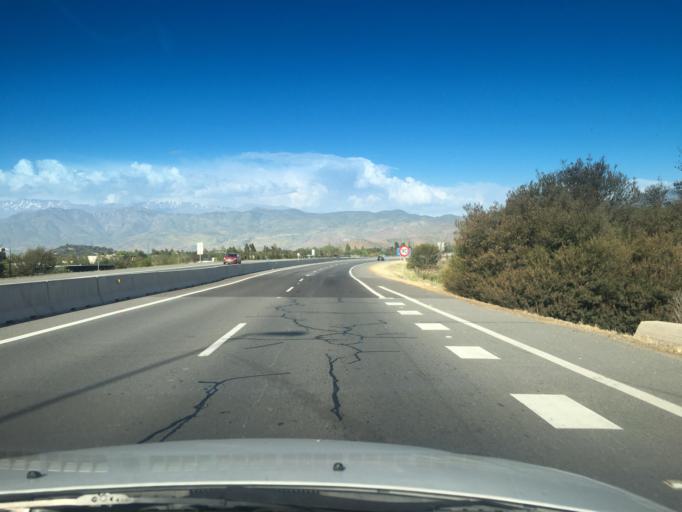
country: CL
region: Santiago Metropolitan
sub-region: Provincia de Chacabuco
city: Chicureo Abajo
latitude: -33.2922
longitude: -70.6989
